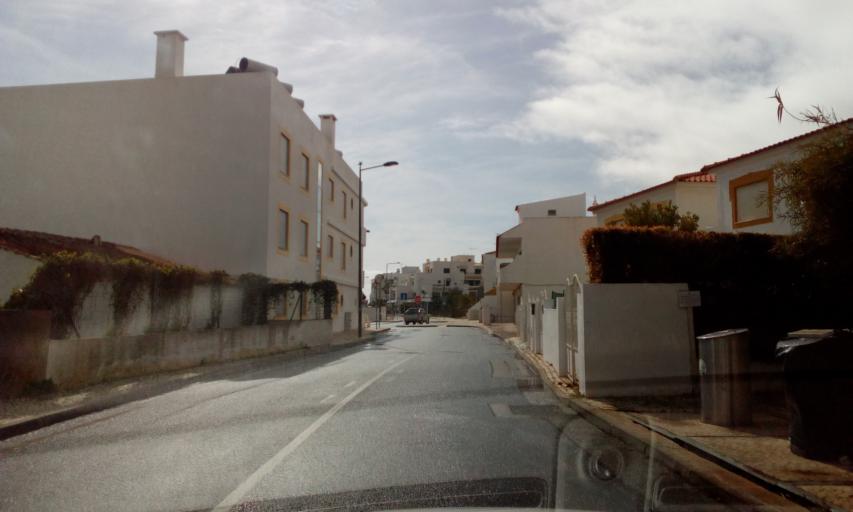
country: PT
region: Faro
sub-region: Albufeira
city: Albufeira
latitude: 37.0917
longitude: -8.1942
